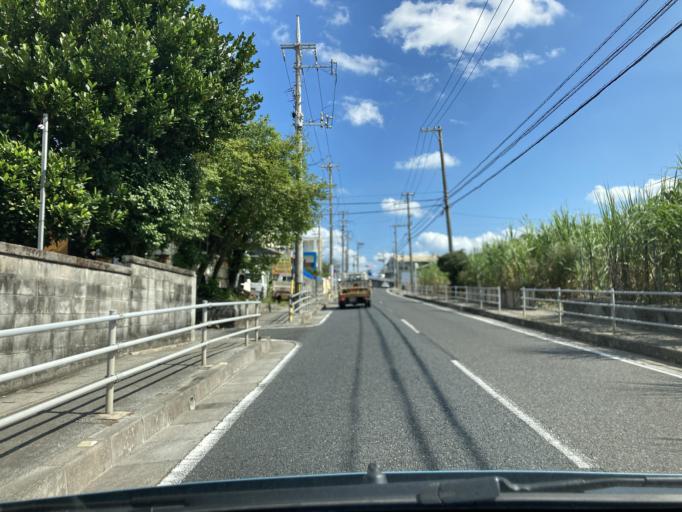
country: JP
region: Okinawa
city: Tomigusuku
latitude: 26.1859
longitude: 127.7187
